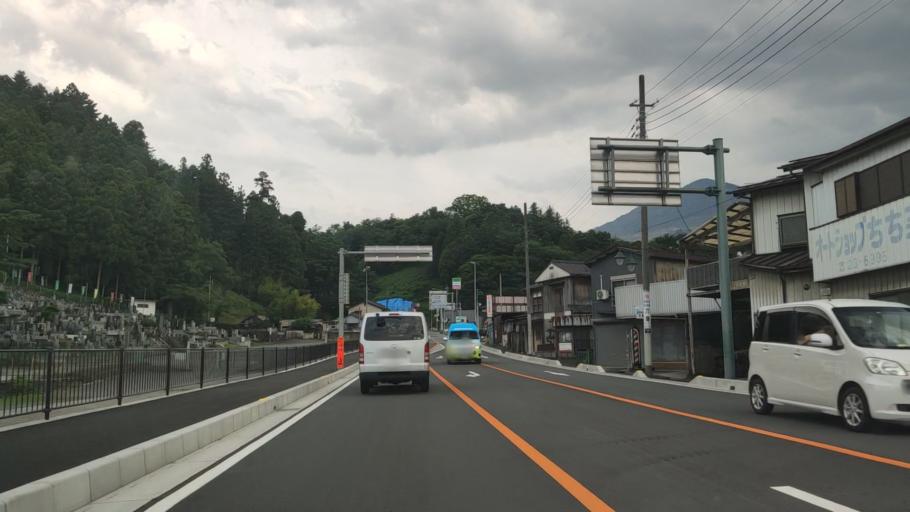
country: JP
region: Saitama
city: Chichibu
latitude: 35.9937
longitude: 139.0896
